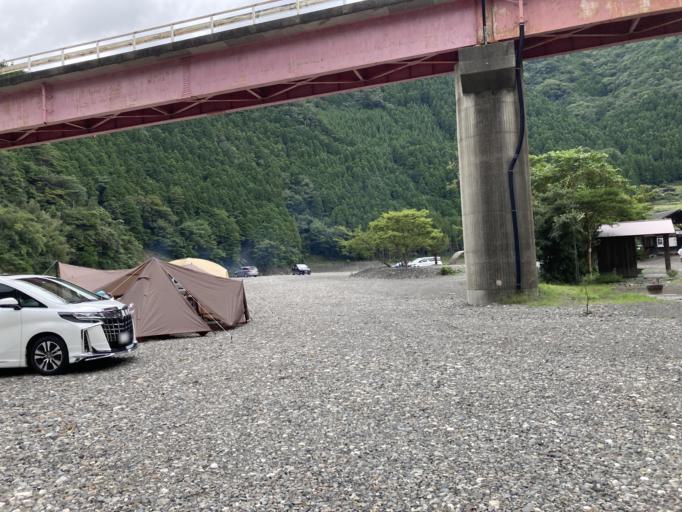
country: JP
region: Wakayama
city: Koya
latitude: 34.1052
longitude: 135.7656
